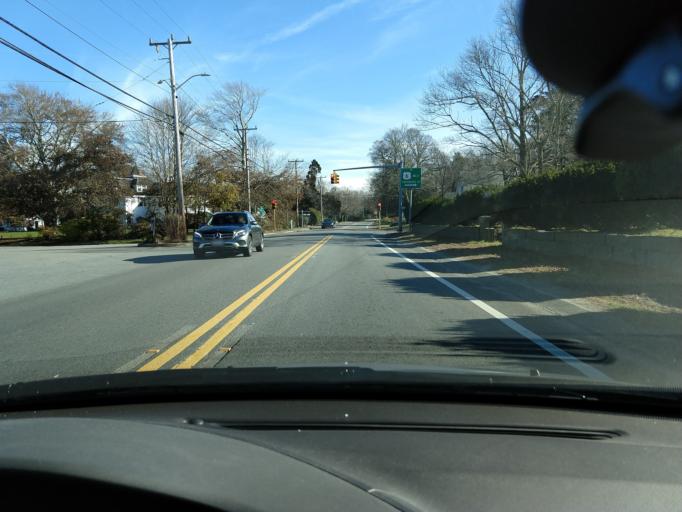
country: US
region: Massachusetts
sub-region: Barnstable County
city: Sagamore
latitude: 41.7720
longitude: -70.5344
